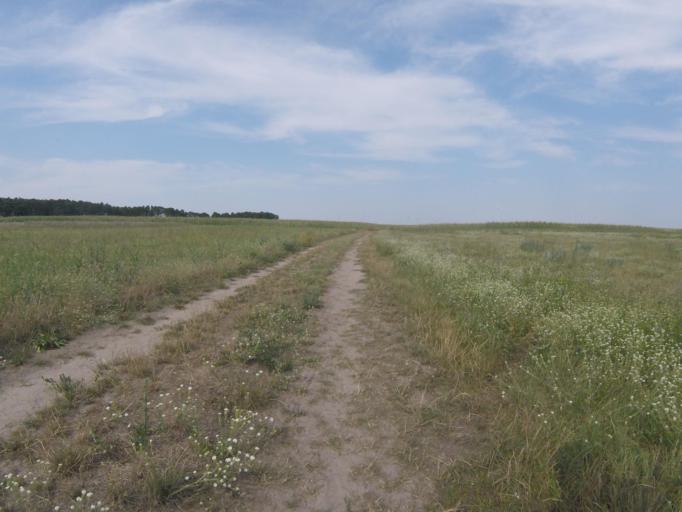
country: DE
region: Brandenburg
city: Bestensee
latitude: 52.3013
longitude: 13.7220
